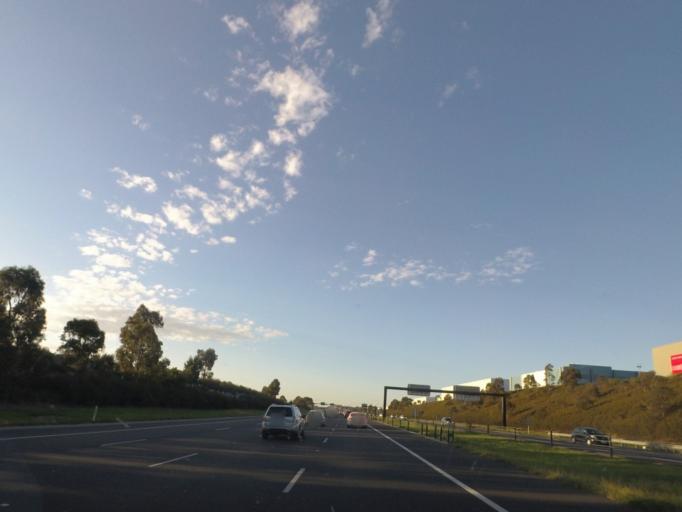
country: AU
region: Victoria
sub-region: Monash
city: Mulgrave
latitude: -37.9119
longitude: 145.2160
